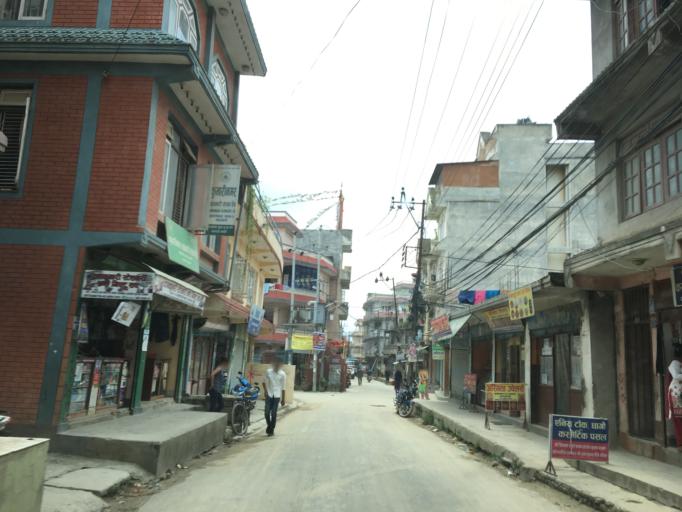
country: NP
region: Central Region
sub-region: Bagmati Zone
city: Kathmandu
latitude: 27.7294
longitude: 85.3538
